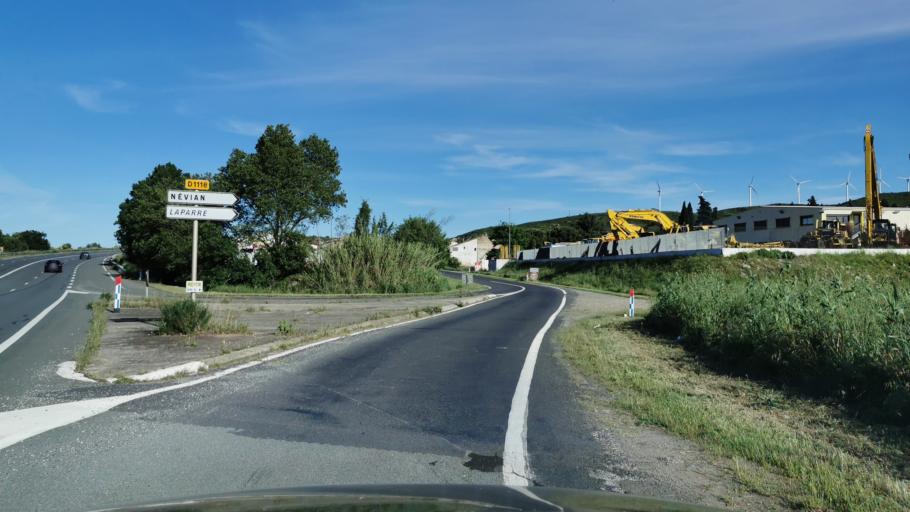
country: FR
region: Languedoc-Roussillon
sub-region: Departement de l'Aude
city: Canet
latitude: 43.2122
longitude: 2.8699
